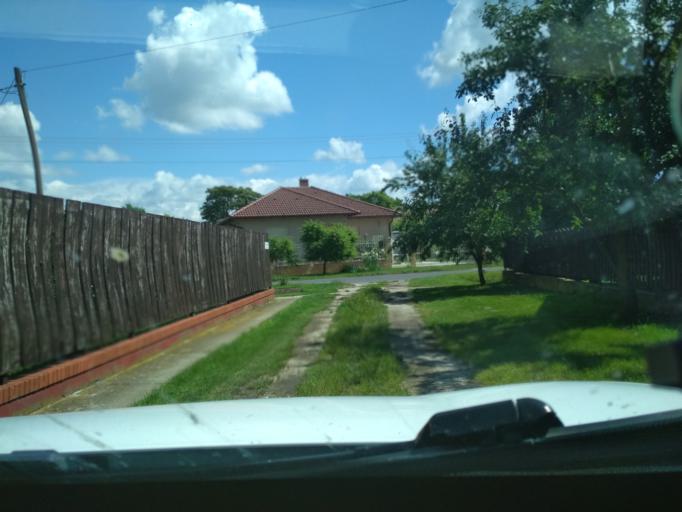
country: HU
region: Jasz-Nagykun-Szolnok
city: Abadszalok
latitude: 47.4839
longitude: 20.5985
